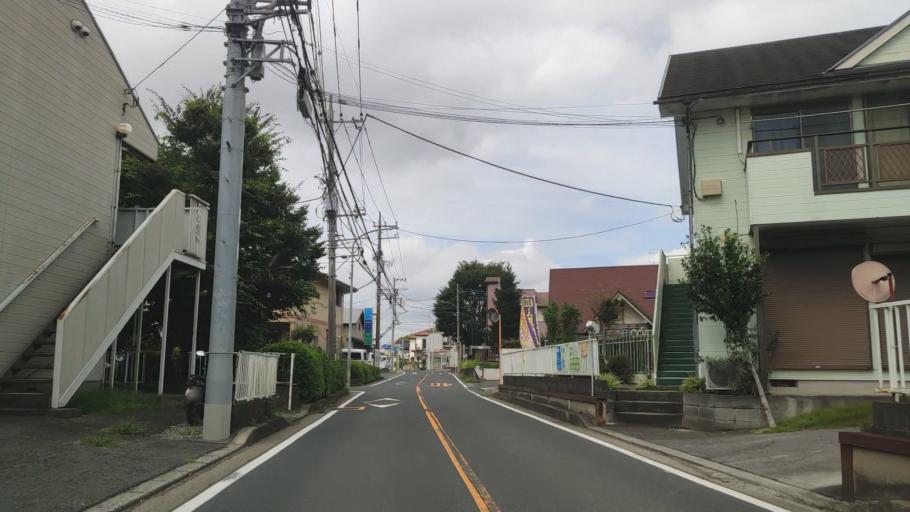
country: JP
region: Kanagawa
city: Minami-rinkan
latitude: 35.4846
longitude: 139.4744
